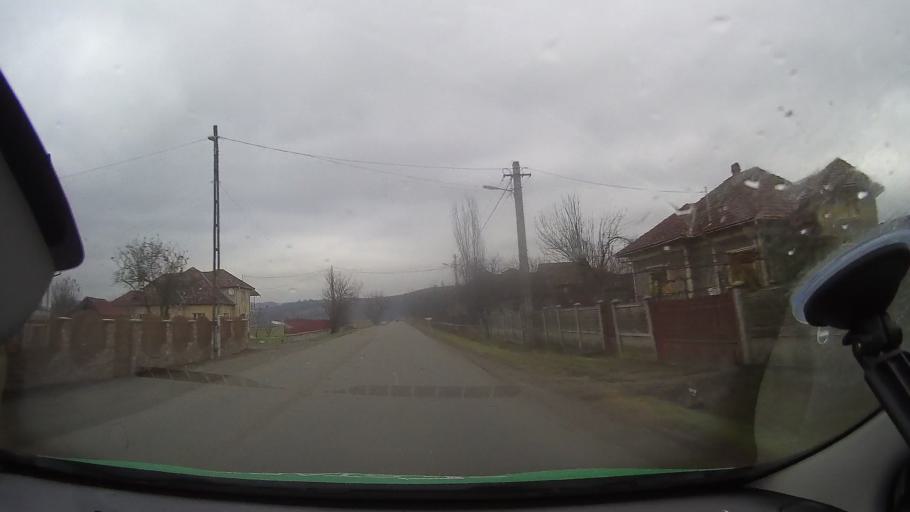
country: RO
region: Hunedoara
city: Vata de Jos
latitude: 46.1870
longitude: 22.6063
